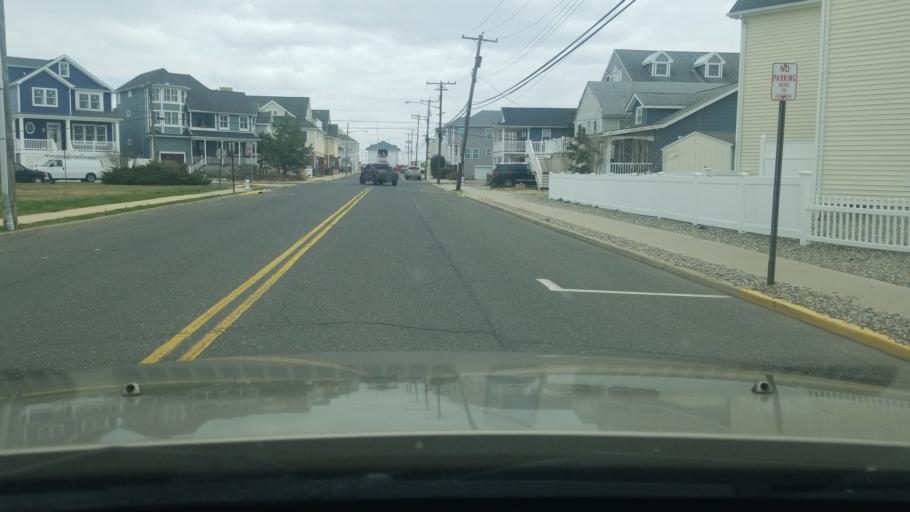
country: US
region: New Jersey
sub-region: Monmouth County
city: Sea Girt
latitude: 40.1130
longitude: -74.0355
